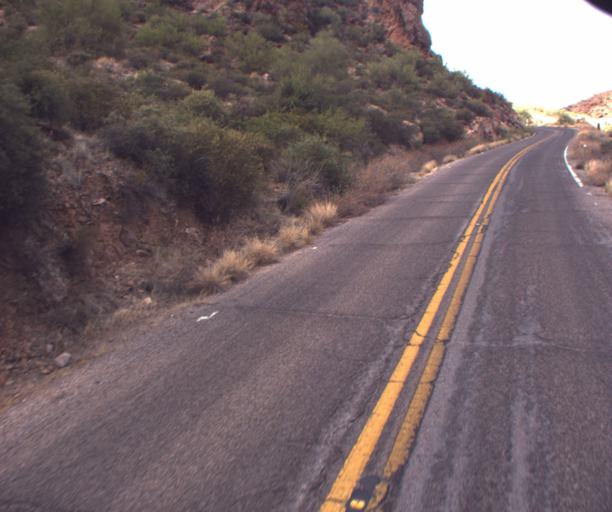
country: US
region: Arizona
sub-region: Pinal County
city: Apache Junction
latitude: 33.5269
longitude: -111.3976
